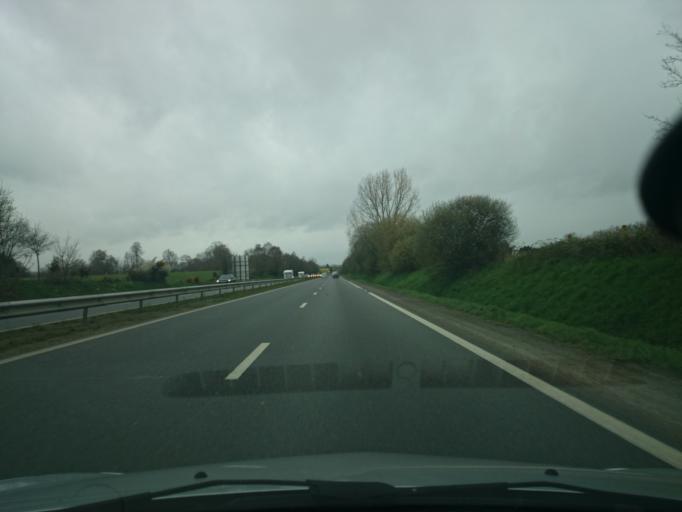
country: FR
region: Brittany
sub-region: Departement des Cotes-d'Armor
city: Plestan
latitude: 48.4254
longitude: -2.4560
